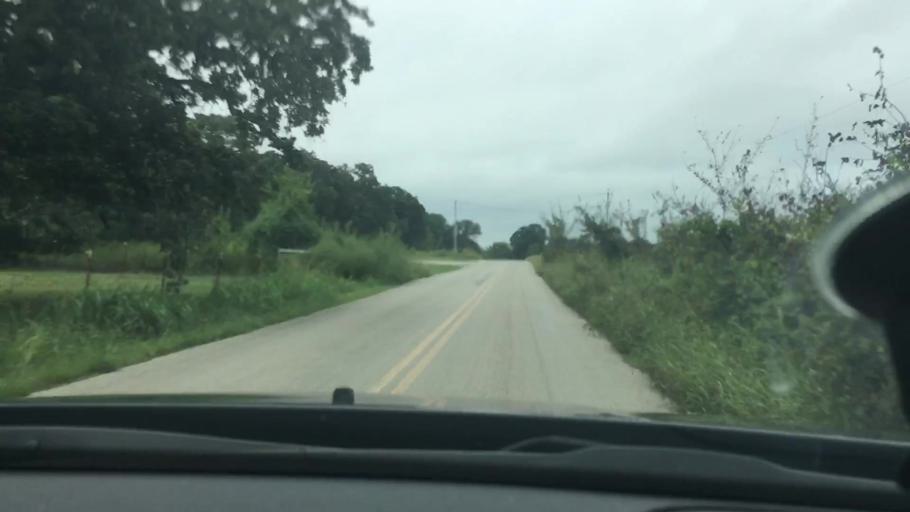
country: US
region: Oklahoma
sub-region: Pontotoc County
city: Ada
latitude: 34.8069
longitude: -96.7573
